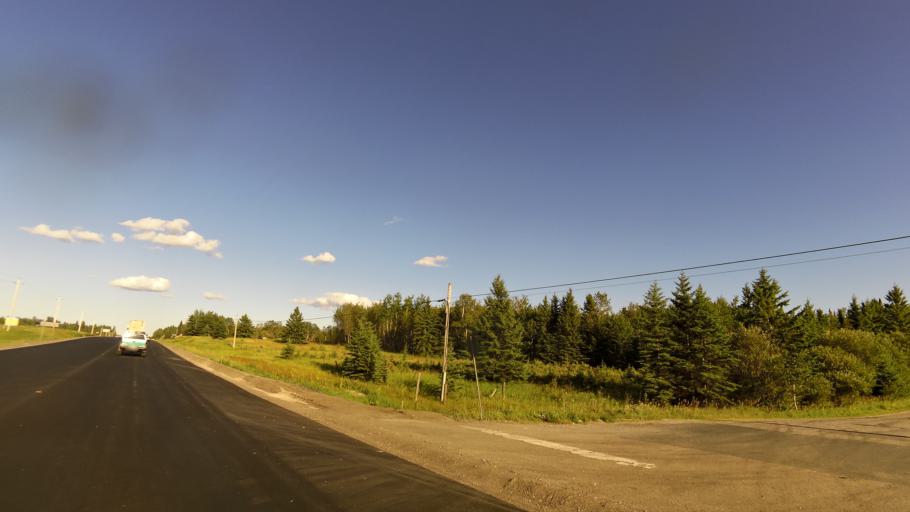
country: CA
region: Ontario
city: Dryden
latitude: 49.8151
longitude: -92.8924
